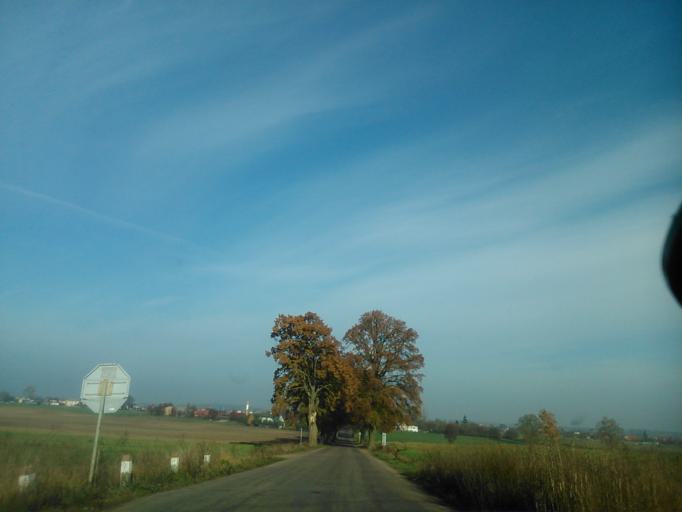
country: PL
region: Warmian-Masurian Voivodeship
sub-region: Powiat dzialdowski
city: Rybno
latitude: 53.2669
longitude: 19.9982
